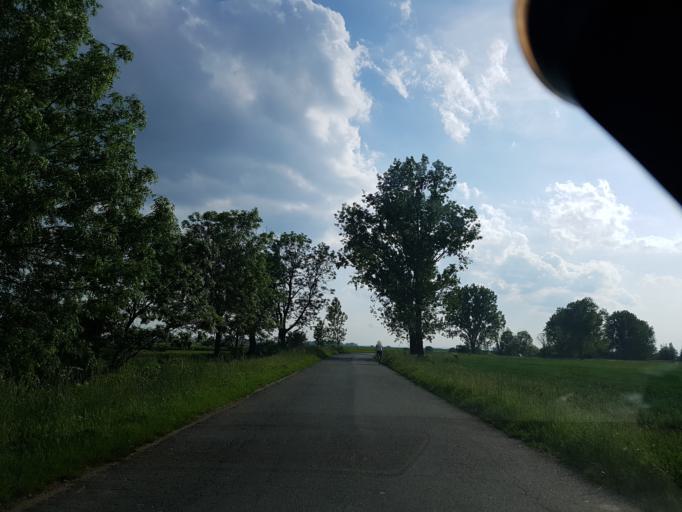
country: PL
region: Lower Silesian Voivodeship
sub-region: Powiat strzelinski
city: Wiazow
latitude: 50.8412
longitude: 17.2269
